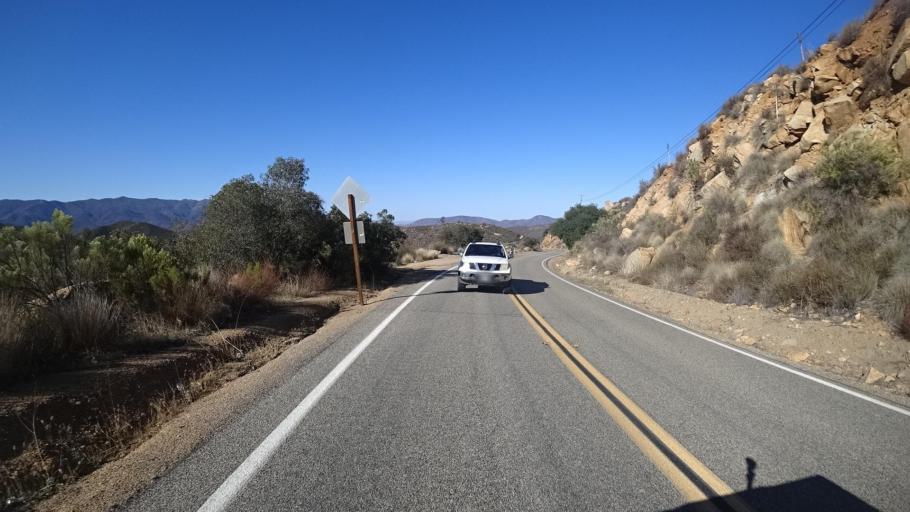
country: US
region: California
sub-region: San Diego County
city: Jamul
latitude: 32.6727
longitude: -116.7664
